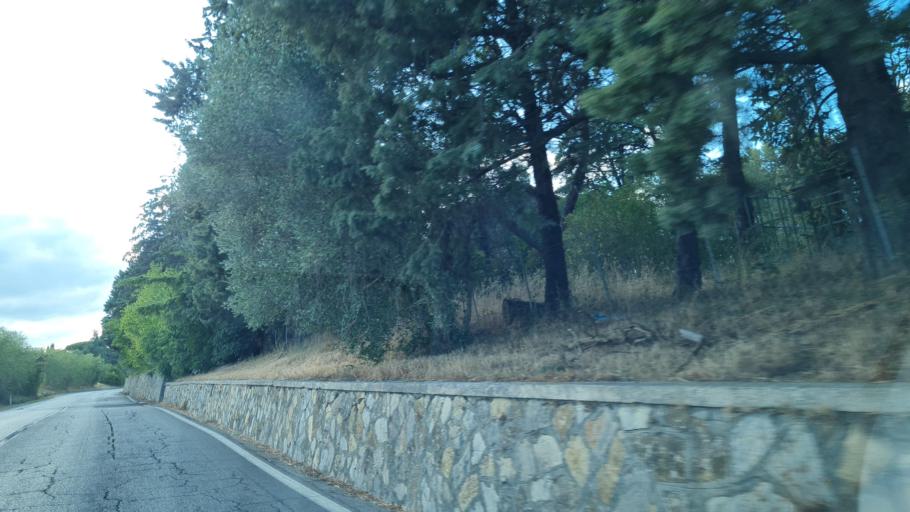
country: IT
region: Tuscany
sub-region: Provincia di Siena
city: Chianciano Terme
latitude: 43.0342
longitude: 11.8453
